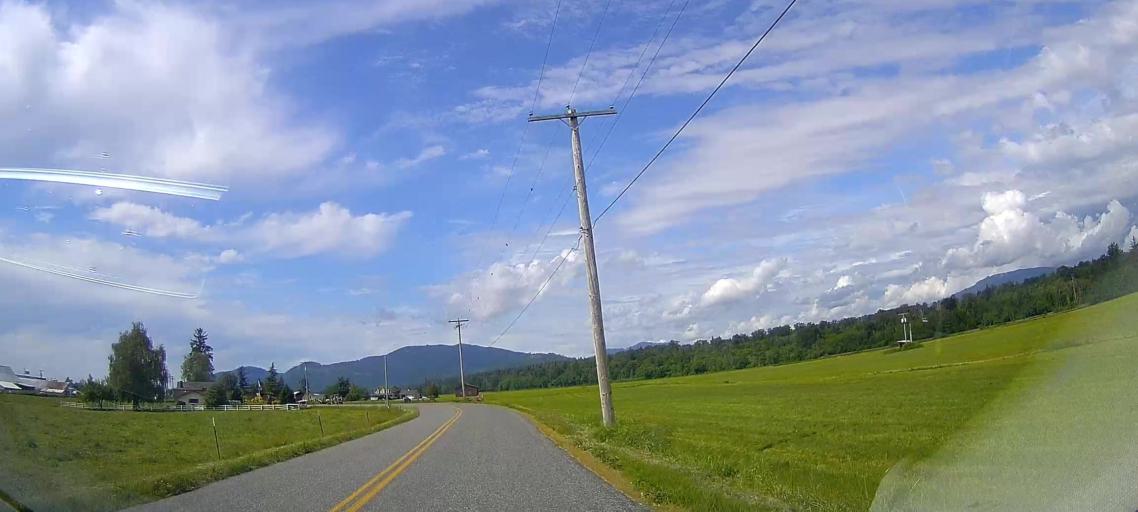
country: US
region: Washington
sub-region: Skagit County
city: Burlington
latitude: 48.5383
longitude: -122.3884
